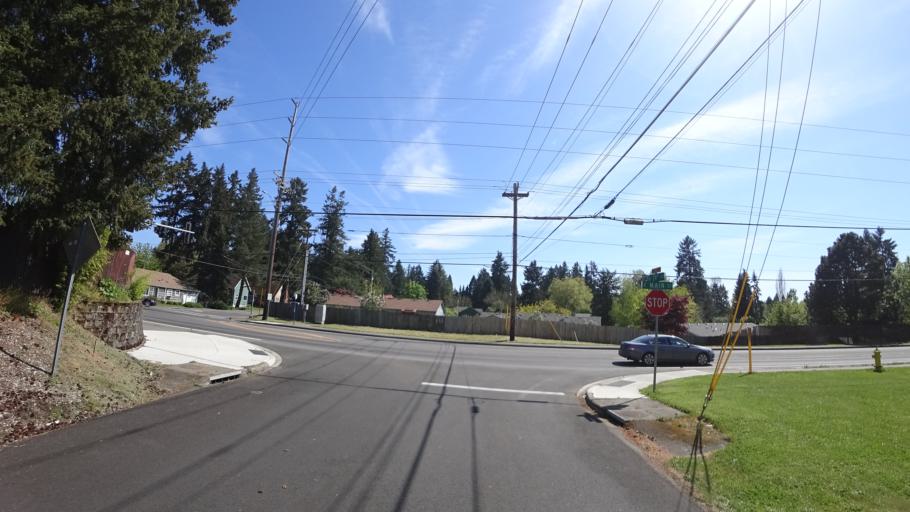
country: US
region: Oregon
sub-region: Washington County
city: Hillsboro
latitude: 45.5213
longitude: -122.9585
